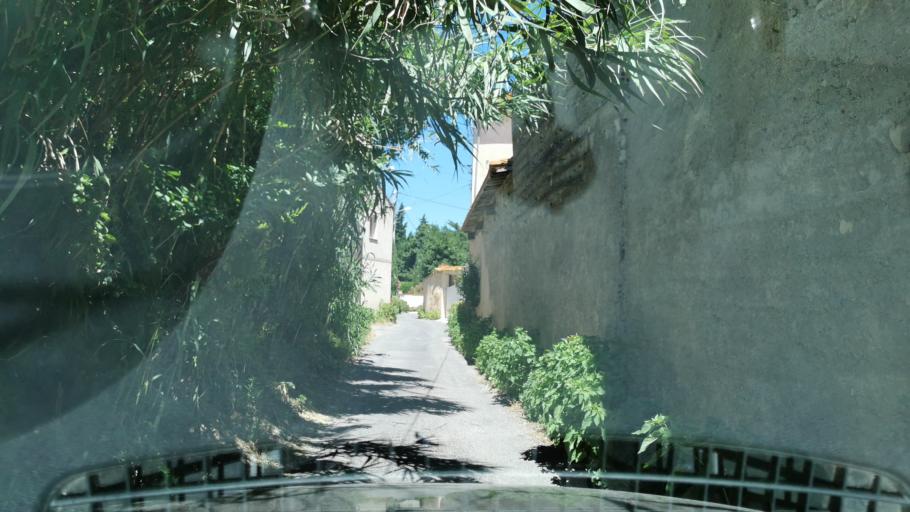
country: FR
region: Languedoc-Roussillon
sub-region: Departement de l'Aude
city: Peyriac-de-Mer
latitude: 43.0921
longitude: 2.9582
